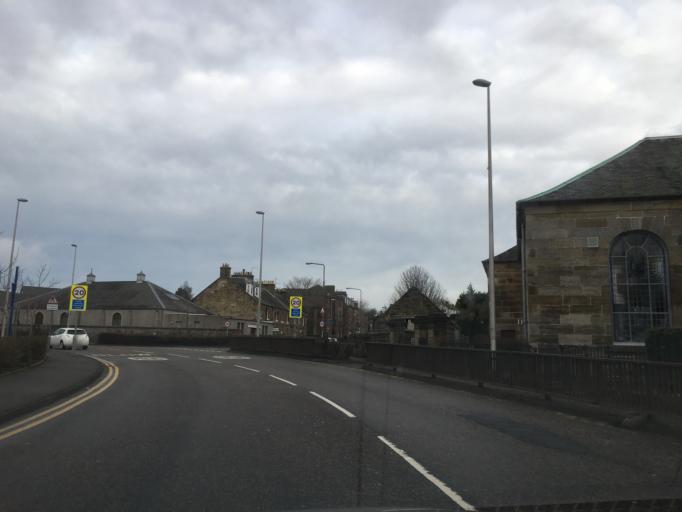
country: GB
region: Scotland
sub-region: Midlothian
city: Penicuik
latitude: 55.8267
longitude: -3.2203
